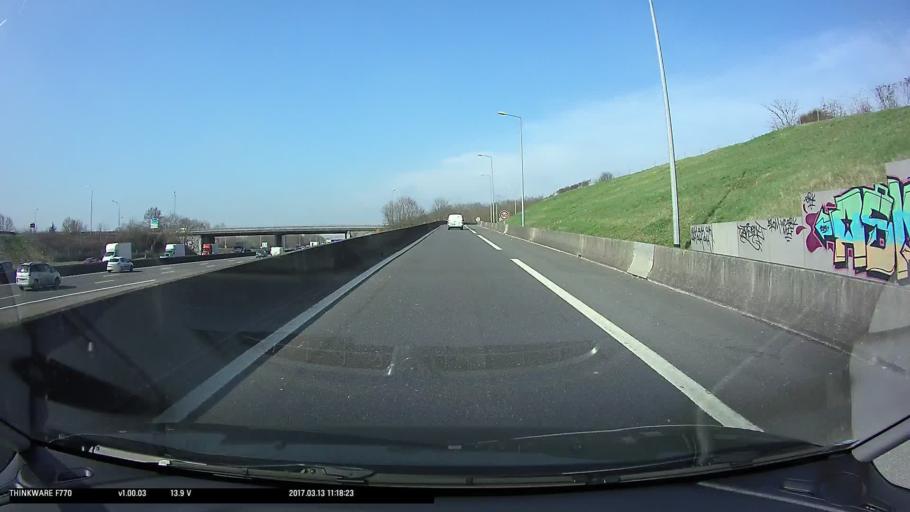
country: FR
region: Ile-de-France
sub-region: Departement de Seine-et-Marne
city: Champs-sur-Marne
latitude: 48.8350
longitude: 2.5845
